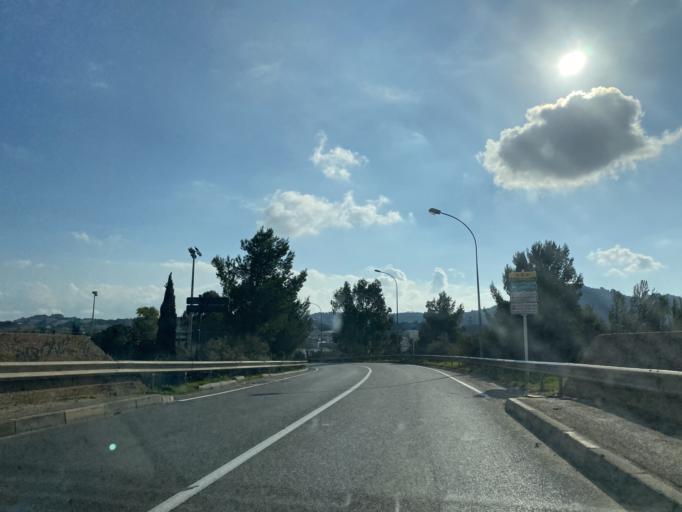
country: FR
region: Provence-Alpes-Cote d'Azur
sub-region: Departement du Var
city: Ollioules
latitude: 43.1188
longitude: 5.8472
